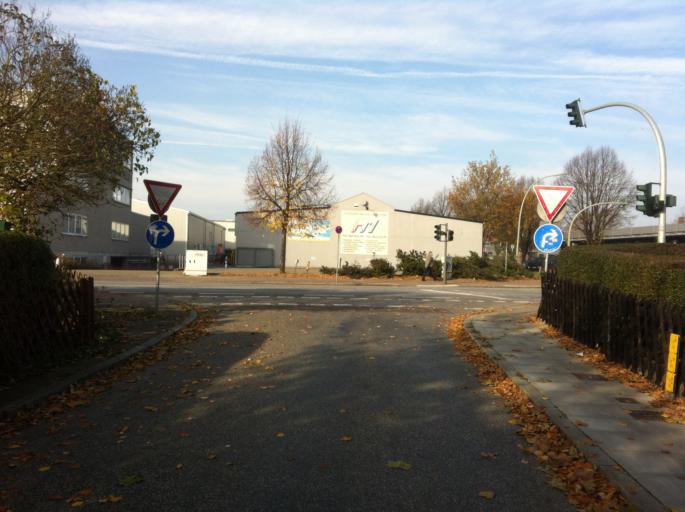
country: DE
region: Hamburg
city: Altona
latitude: 53.5689
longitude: 9.9288
